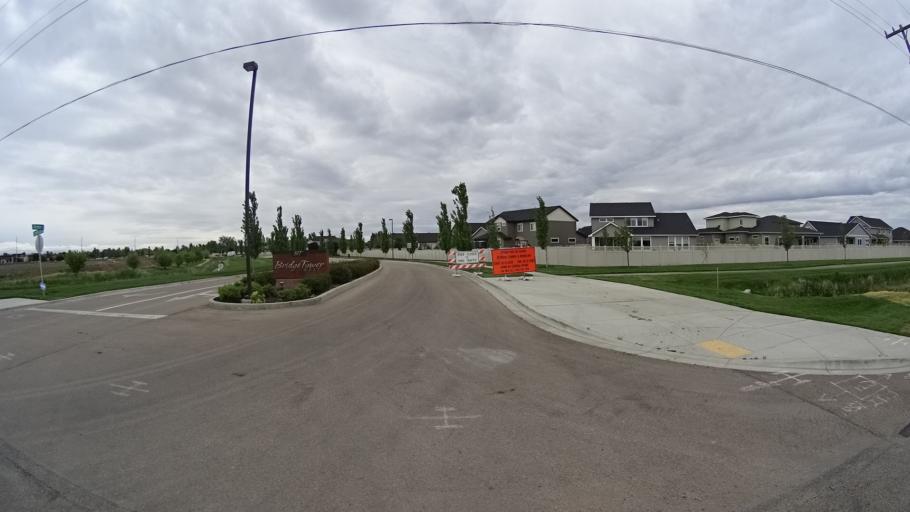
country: US
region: Idaho
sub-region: Ada County
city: Meridian
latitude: 43.6485
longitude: -116.4376
